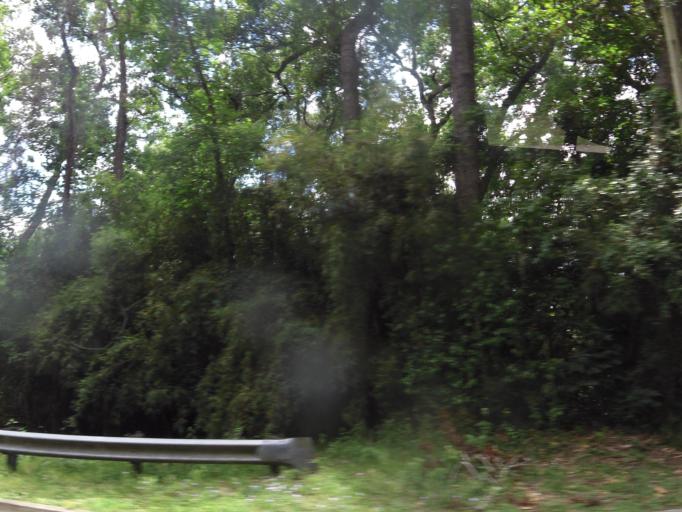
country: US
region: Florida
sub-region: Clay County
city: Orange Park
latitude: 30.1884
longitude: -81.6973
